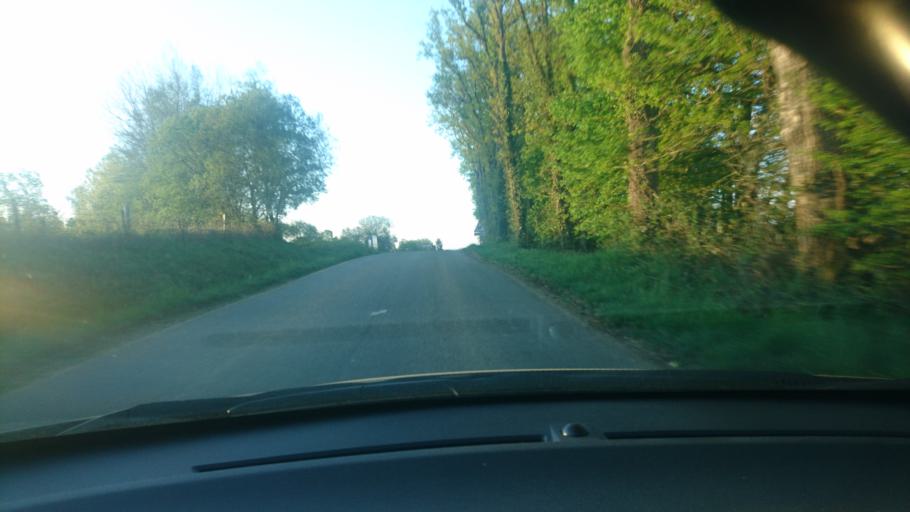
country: FR
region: Limousin
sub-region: Departement de la Haute-Vienne
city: Boisseuil
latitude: 45.7407
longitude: 1.3216
